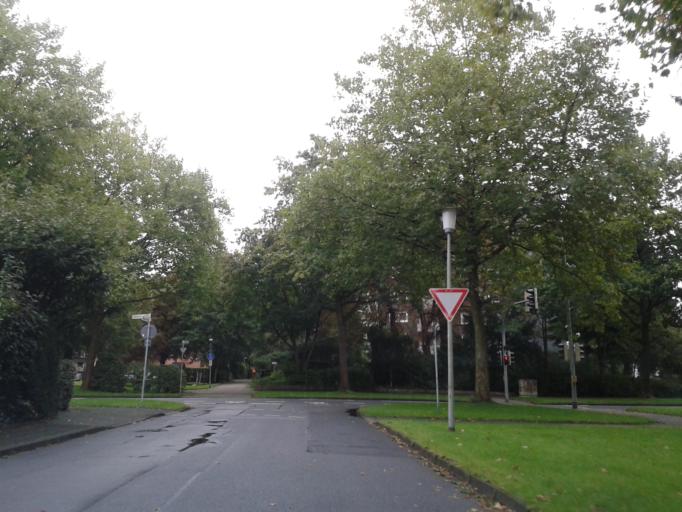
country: DE
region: North Rhine-Westphalia
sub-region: Regierungsbezirk Detmold
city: Paderborn
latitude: 51.7413
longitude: 8.7482
